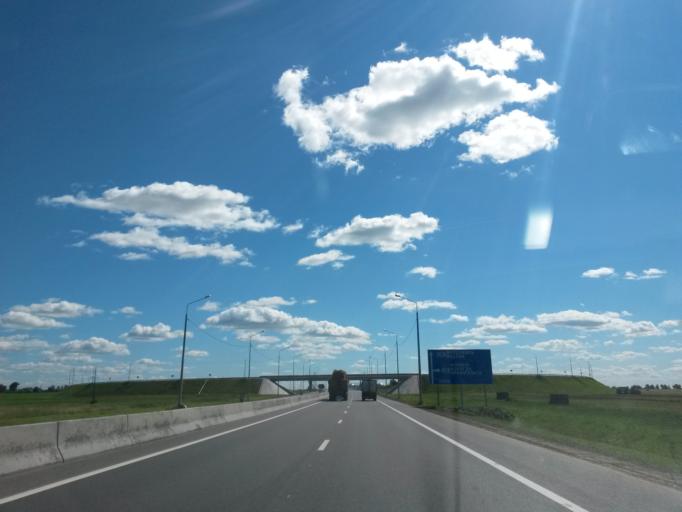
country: RU
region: Jaroslavl
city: Yaroslavl
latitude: 57.7263
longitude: 39.8995
